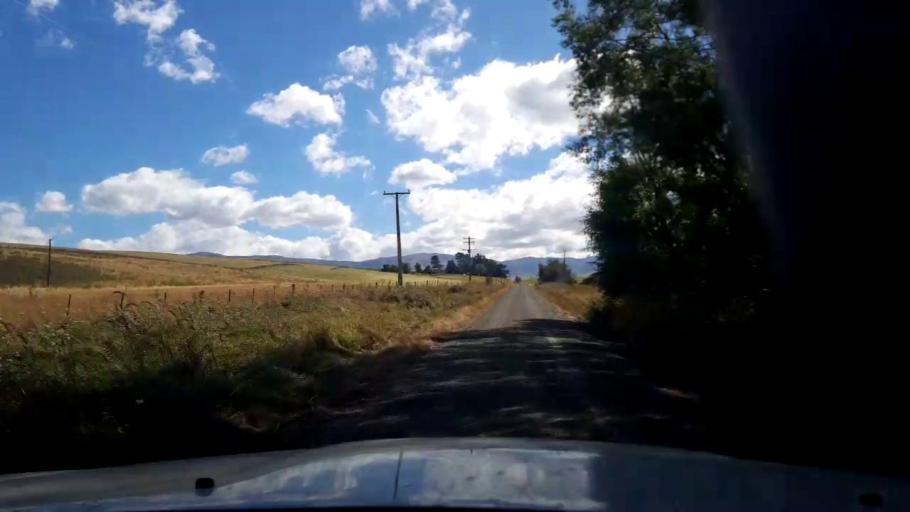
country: NZ
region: Canterbury
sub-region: Timaru District
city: Pleasant Point
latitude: -44.2388
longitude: 170.8643
